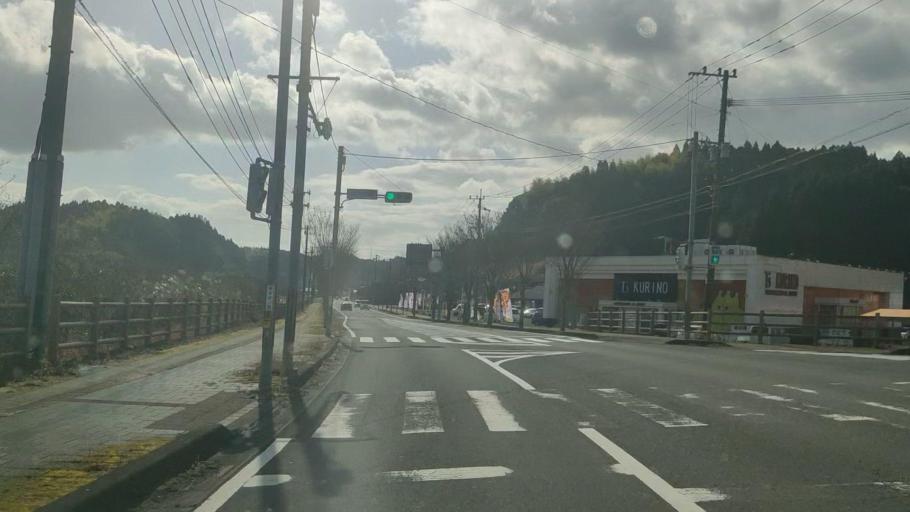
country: JP
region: Kagoshima
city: Okuchi-shinohara
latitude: 31.9474
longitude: 130.7116
